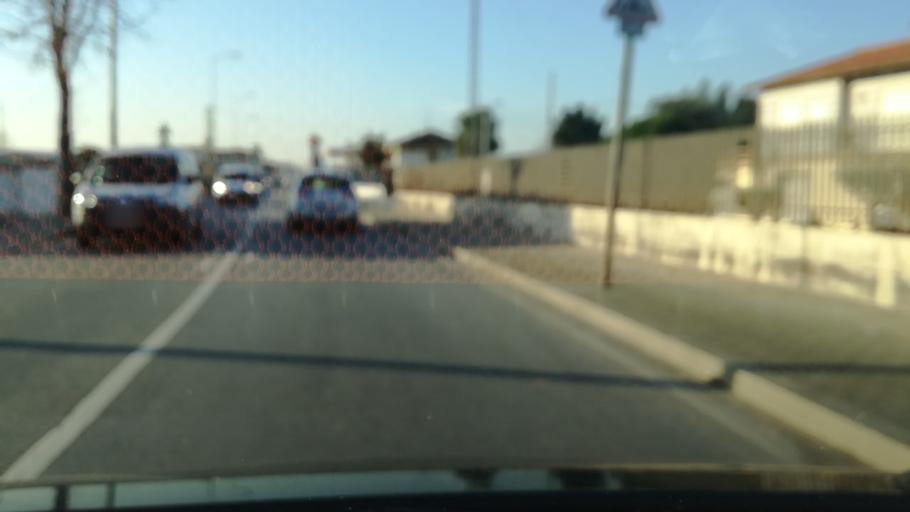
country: PT
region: Porto
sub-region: Trofa
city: Bougado
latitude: 41.3367
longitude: -8.5316
